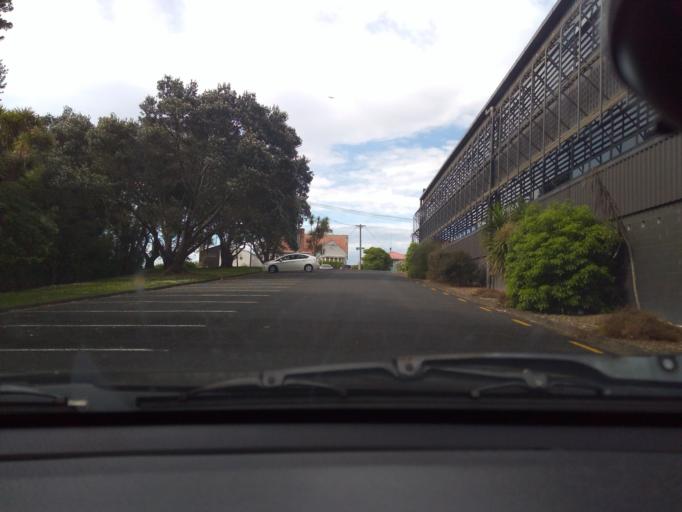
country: NZ
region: Auckland
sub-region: Auckland
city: Waitakere
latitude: -36.9075
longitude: 174.6809
